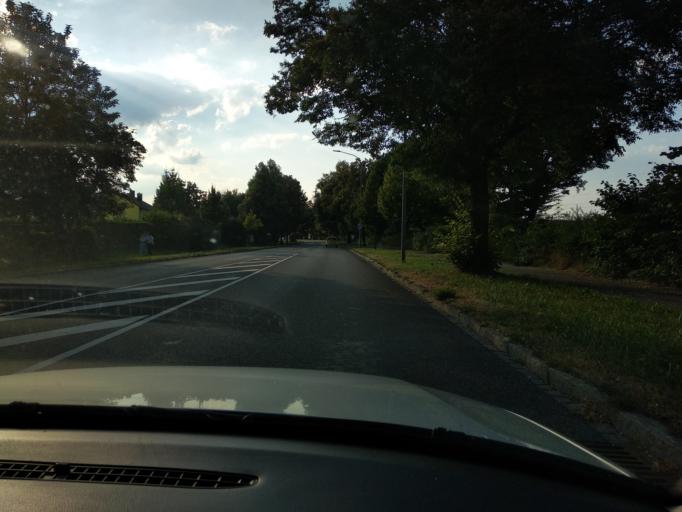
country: DE
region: Bavaria
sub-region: Swabia
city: Memmingen
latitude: 47.9961
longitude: 10.1941
